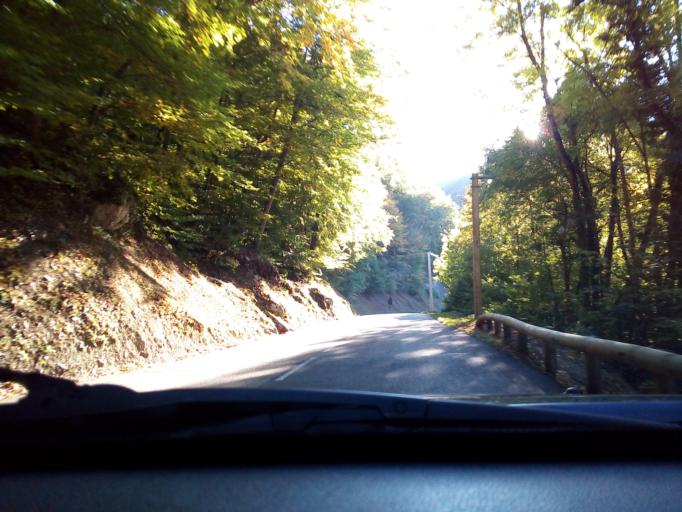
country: FR
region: Rhone-Alpes
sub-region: Departement de l'Isere
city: Le Sappey-en-Chartreuse
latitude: 45.2425
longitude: 5.7569
